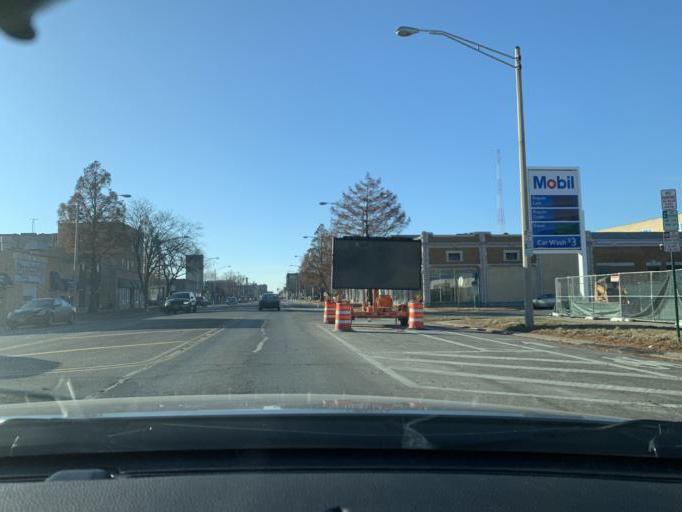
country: US
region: Illinois
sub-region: Cook County
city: Oak Park
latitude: 41.8799
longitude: -87.7906
